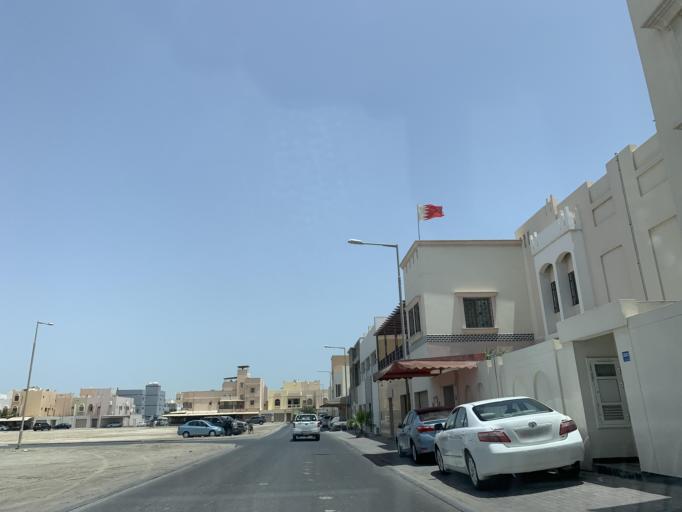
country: BH
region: Northern
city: Sitrah
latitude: 26.1401
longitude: 50.5895
